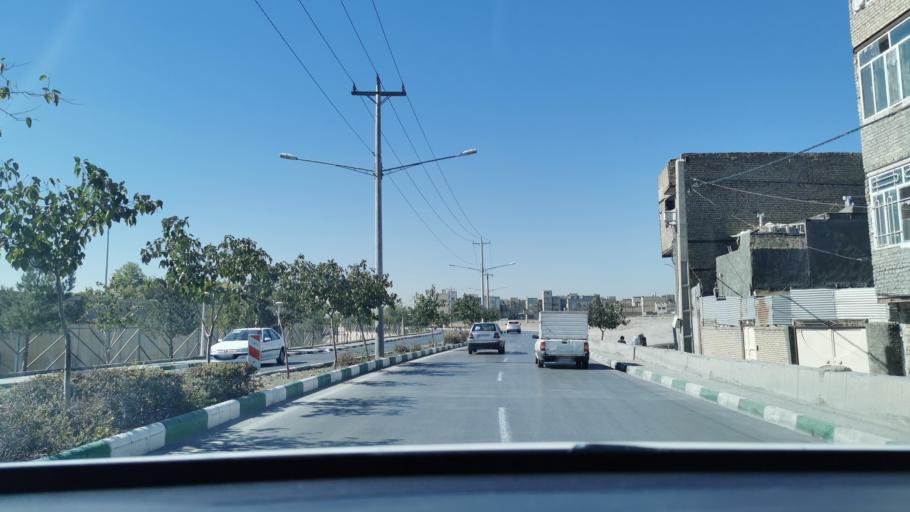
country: IR
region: Razavi Khorasan
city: Mashhad
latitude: 36.3356
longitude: 59.6147
